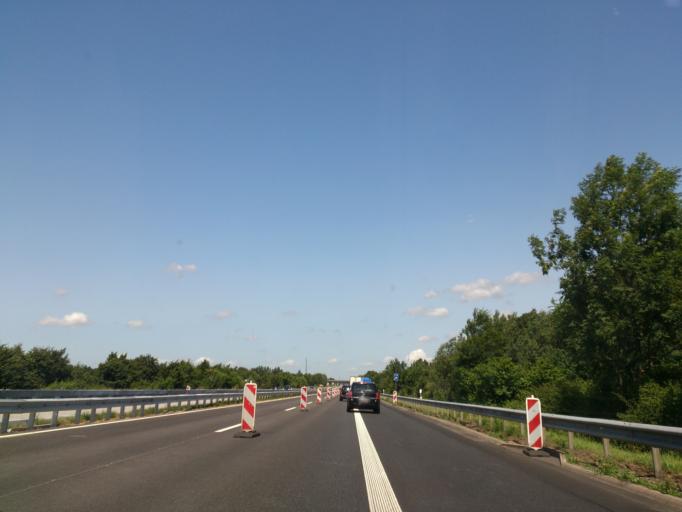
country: DE
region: Schleswig-Holstein
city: Tensbuttel-Rost
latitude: 54.1104
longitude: 9.2621
